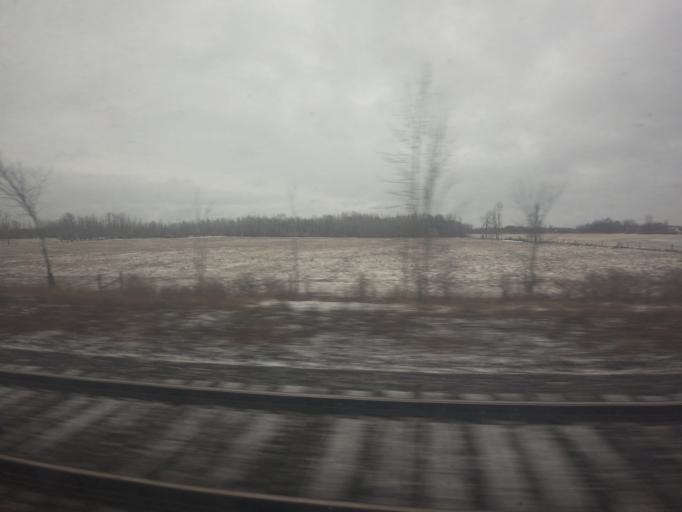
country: CA
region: Ontario
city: Gananoque
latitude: 44.3712
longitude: -76.1309
